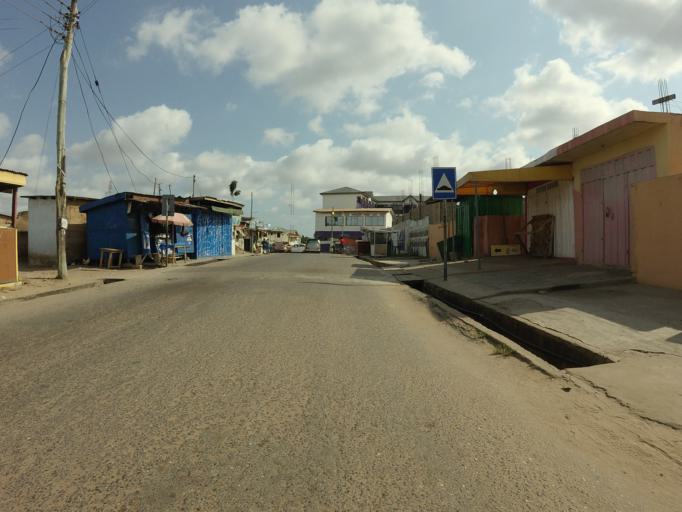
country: GH
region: Greater Accra
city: Dome
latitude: 5.6165
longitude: -0.2363
